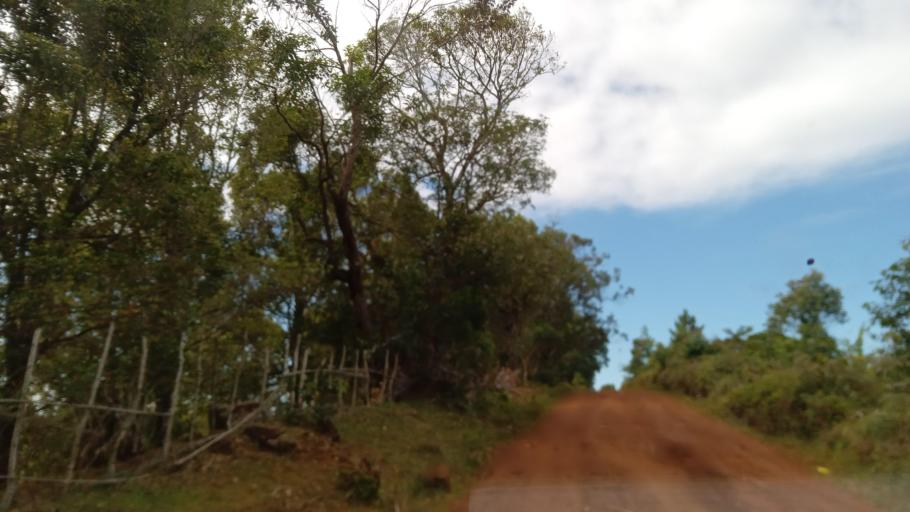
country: MG
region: Atsimo-Atsinanana
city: Vohipaho
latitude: -23.7528
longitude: 47.5547
